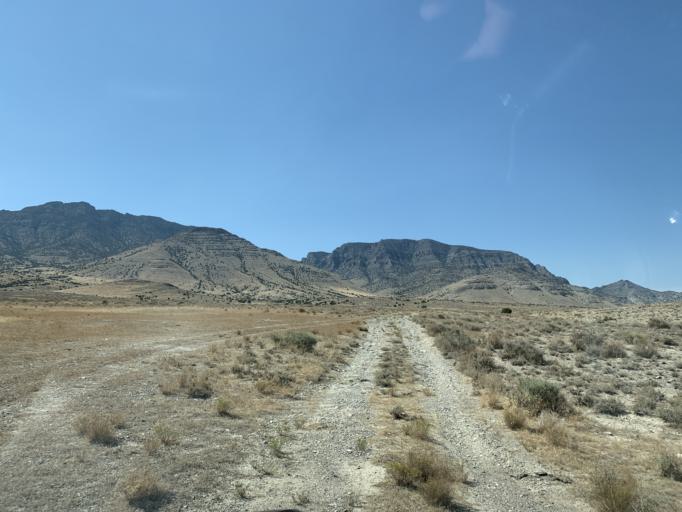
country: US
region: Utah
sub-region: Beaver County
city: Milford
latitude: 38.9759
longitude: -113.4570
